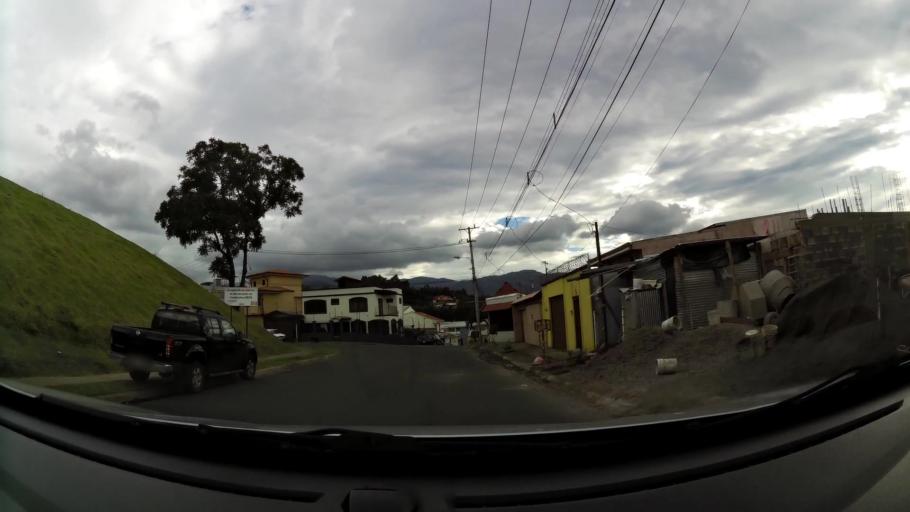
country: CR
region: Heredia
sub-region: Canton de Belen
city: San Antonio
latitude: 9.9673
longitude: -84.1883
